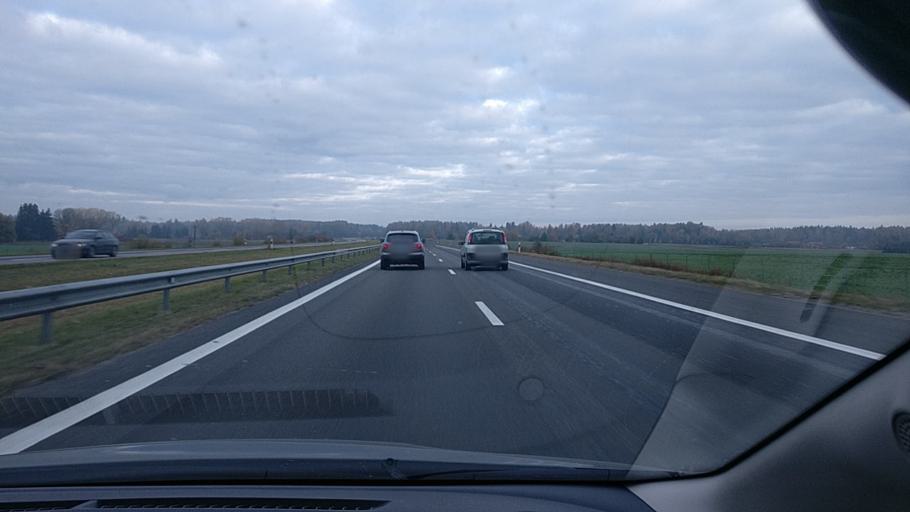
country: LT
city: Sirvintos
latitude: 55.0818
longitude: 24.8750
